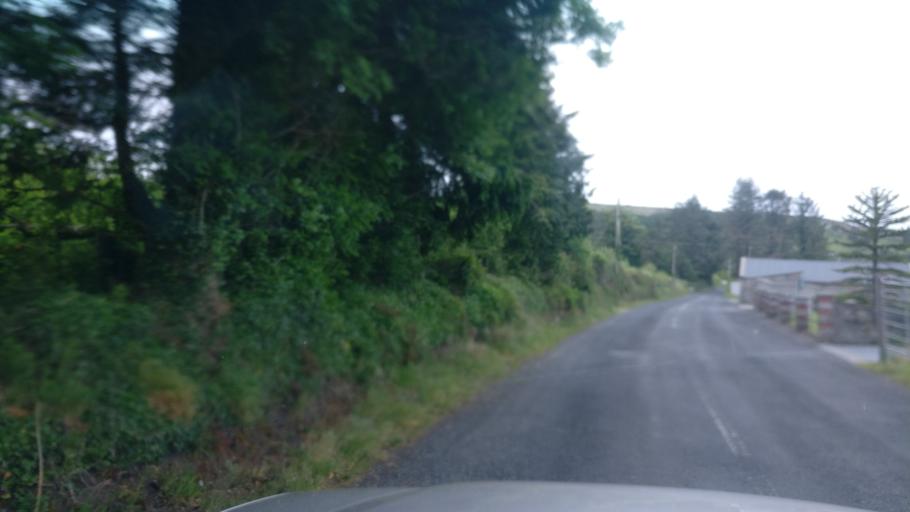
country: IE
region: Connaught
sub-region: County Galway
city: Loughrea
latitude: 53.0579
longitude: -8.6420
